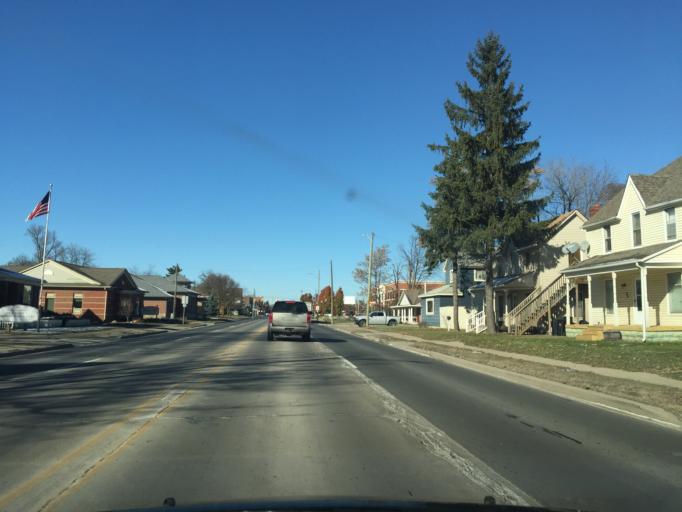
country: US
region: Michigan
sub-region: Oakland County
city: Oxford
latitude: 42.8210
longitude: -83.2615
